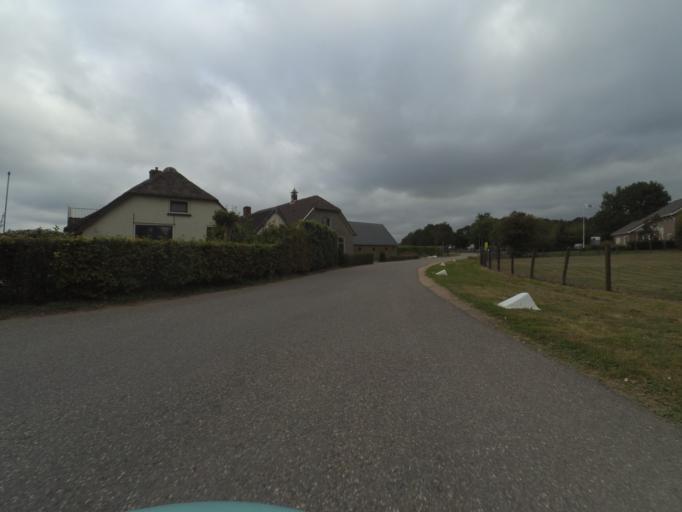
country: NL
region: Gelderland
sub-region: Gemeente Buren
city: Lienden
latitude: 51.9617
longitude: 5.4893
